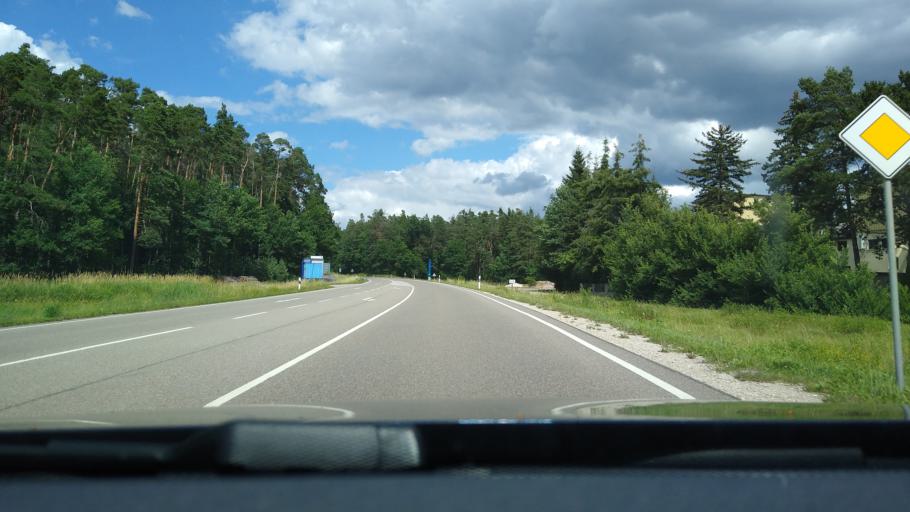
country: DE
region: Bavaria
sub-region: Regierungsbezirk Mittelfranken
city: Gunzenhausen
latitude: 49.1319
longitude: 10.7762
